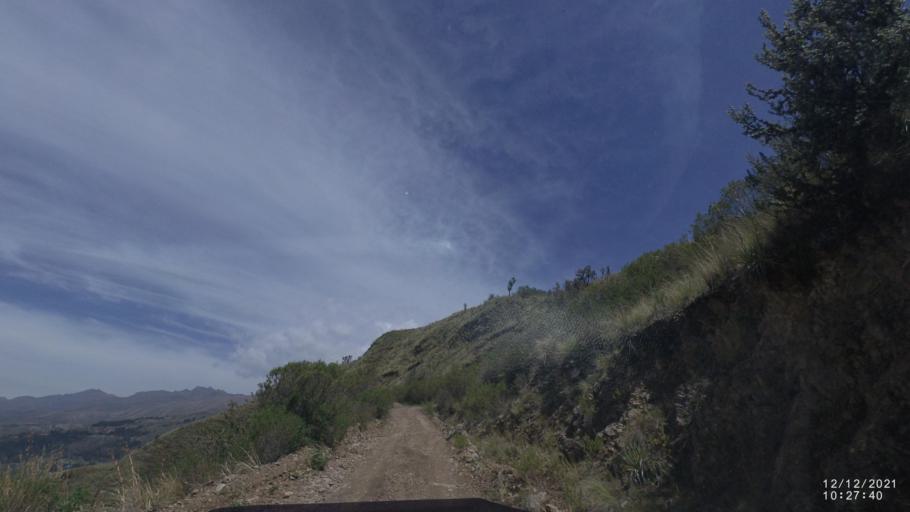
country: BO
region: Cochabamba
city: Cochabamba
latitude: -17.3130
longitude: -66.1884
